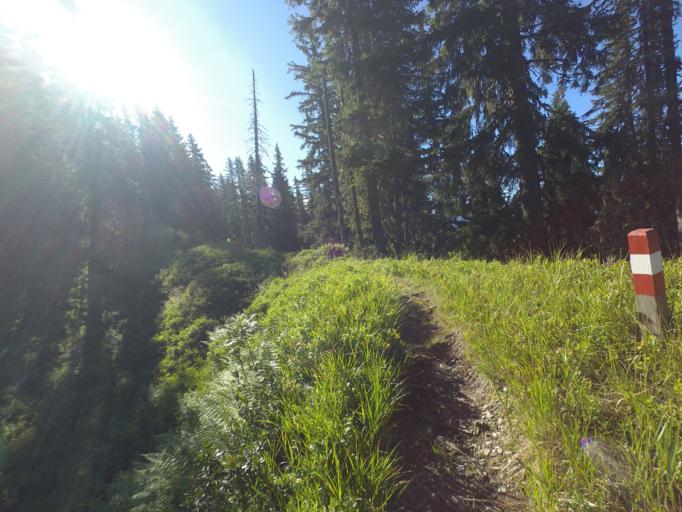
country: AT
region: Salzburg
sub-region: Politischer Bezirk Sankt Johann im Pongau
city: Goldegg
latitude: 47.3627
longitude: 13.0679
